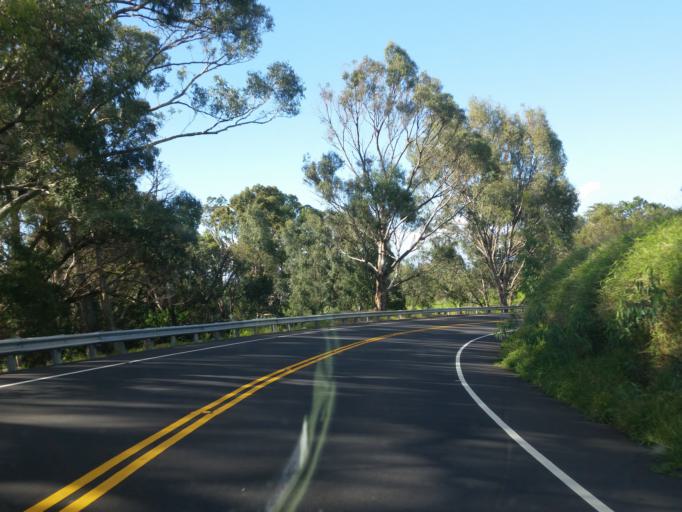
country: US
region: Hawaii
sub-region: Maui County
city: Pukalani
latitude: 20.8246
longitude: -156.3162
